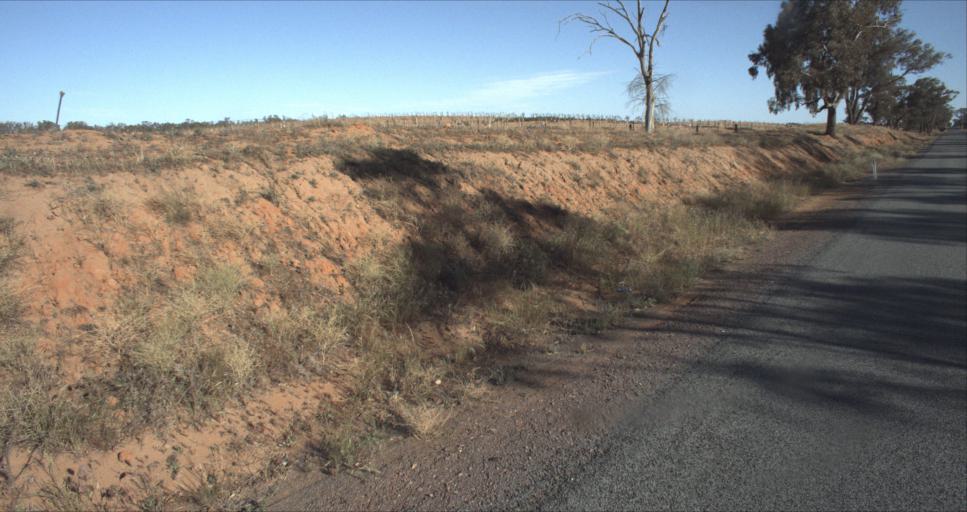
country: AU
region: New South Wales
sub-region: Leeton
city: Leeton
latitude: -34.6481
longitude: 146.3518
